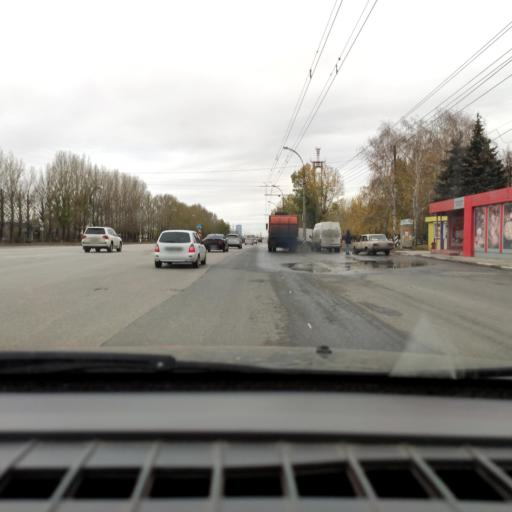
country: RU
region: Samara
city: Tol'yatti
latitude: 53.5245
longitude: 49.2604
